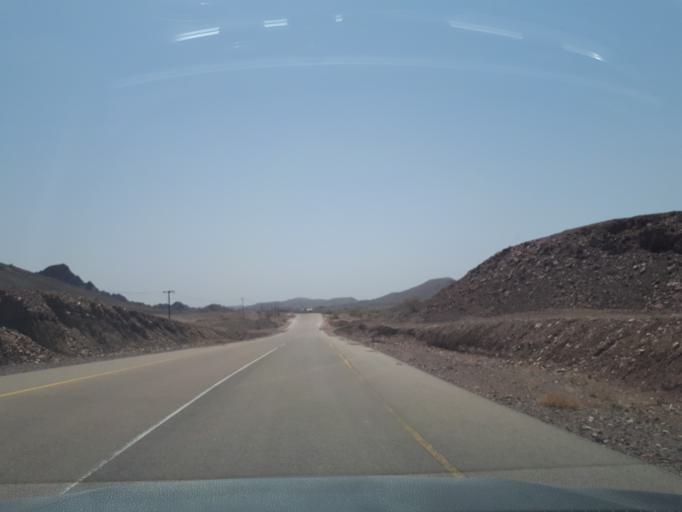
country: OM
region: Ash Sharqiyah
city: Badiyah
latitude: 22.4973
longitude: 59.1021
